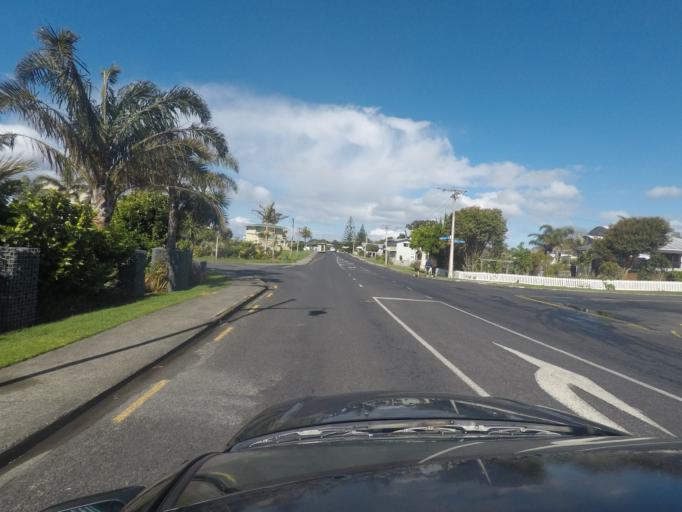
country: NZ
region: Bay of Plenty
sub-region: Western Bay of Plenty District
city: Waihi Beach
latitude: -37.4121
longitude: 175.9443
